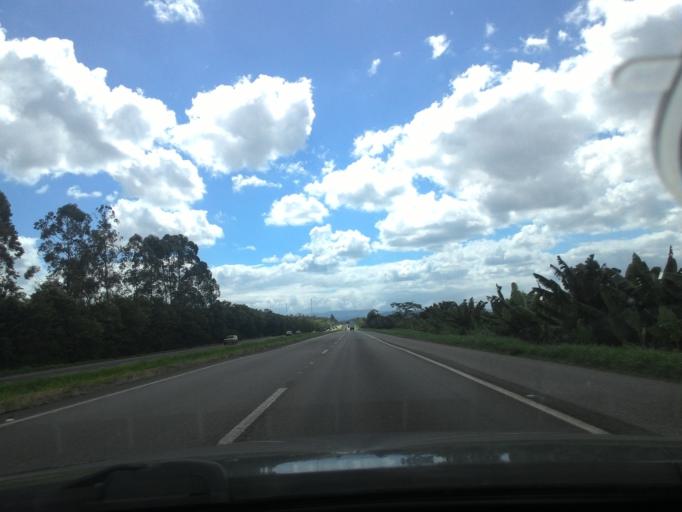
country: BR
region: Sao Paulo
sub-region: Jacupiranga
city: Jacupiranga
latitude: -24.7226
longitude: -48.0521
